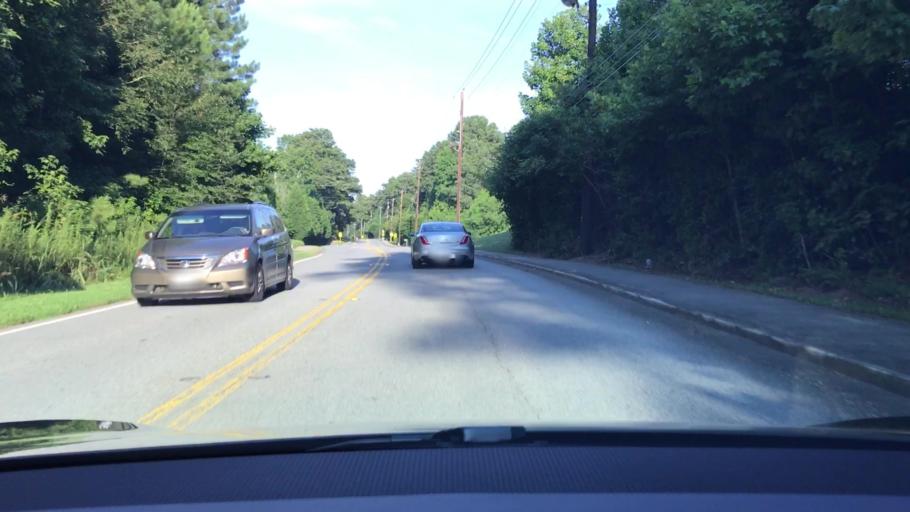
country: US
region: Georgia
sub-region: Fulton County
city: Alpharetta
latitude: 34.0769
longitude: -84.2465
